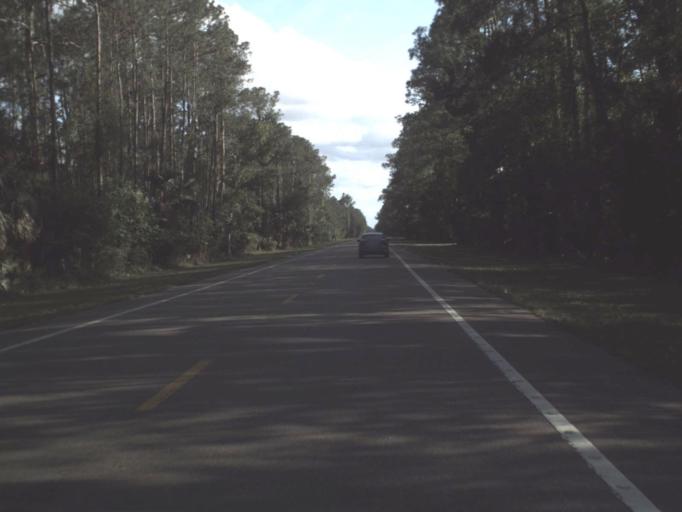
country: US
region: Florida
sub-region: Flagler County
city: Bunnell
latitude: 29.3997
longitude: -81.3071
